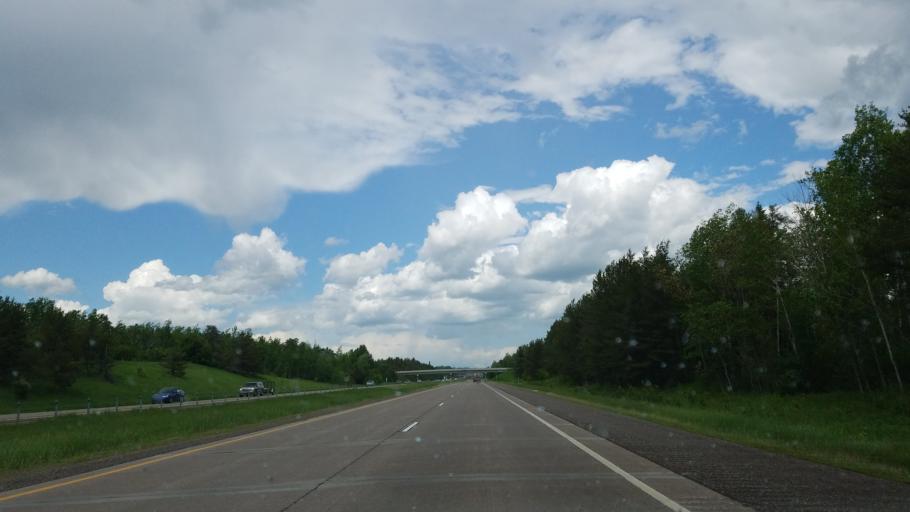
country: US
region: Minnesota
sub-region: Carlton County
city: Moose Lake
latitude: 46.4879
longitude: -92.7030
